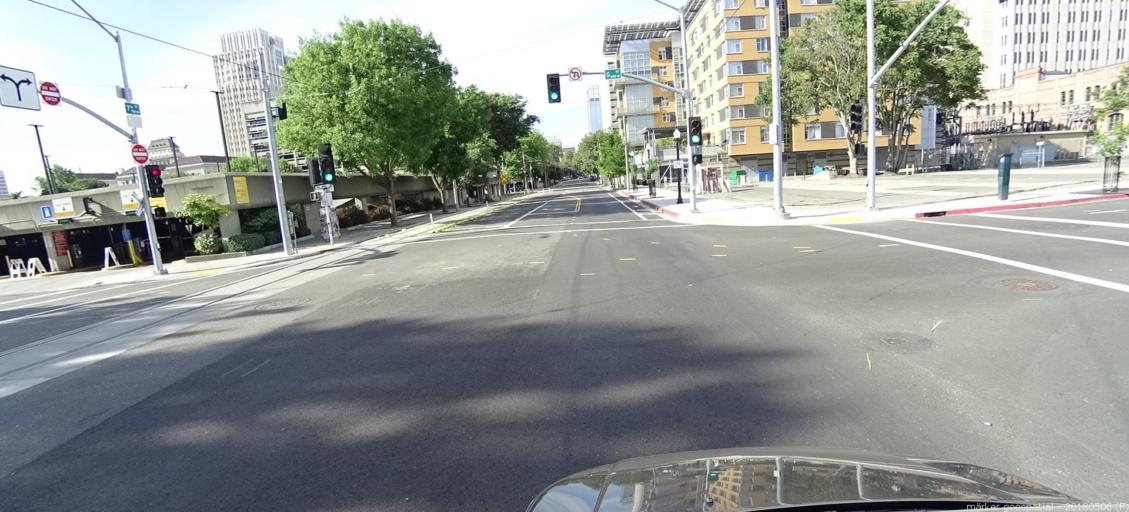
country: US
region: California
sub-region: Sacramento County
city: Sacramento
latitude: 38.5849
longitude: -121.4960
